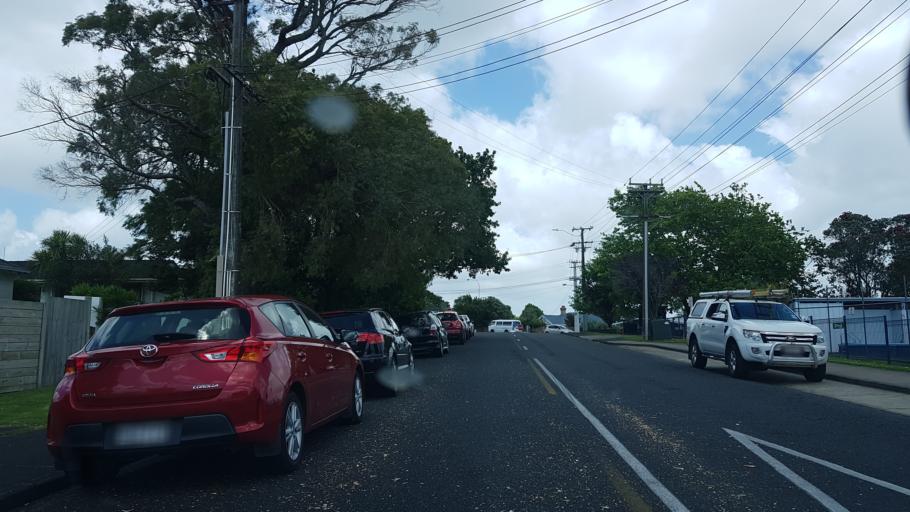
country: NZ
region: Auckland
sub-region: Auckland
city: North Shore
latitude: -36.8003
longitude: 174.7037
